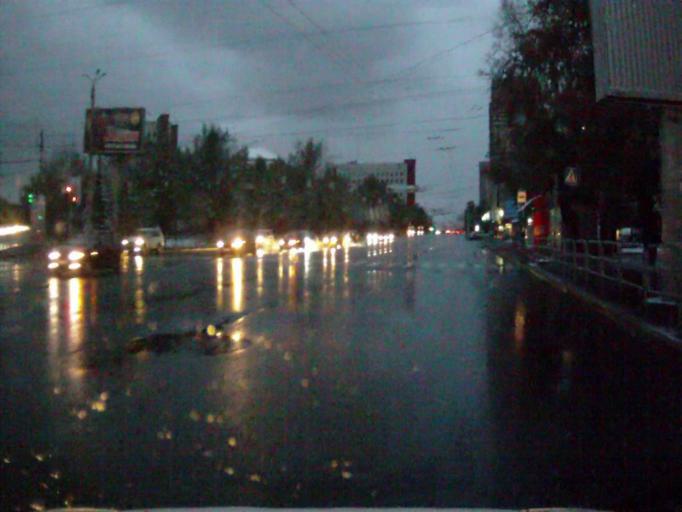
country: RU
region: Chelyabinsk
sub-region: Gorod Chelyabinsk
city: Chelyabinsk
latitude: 55.1516
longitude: 61.3897
